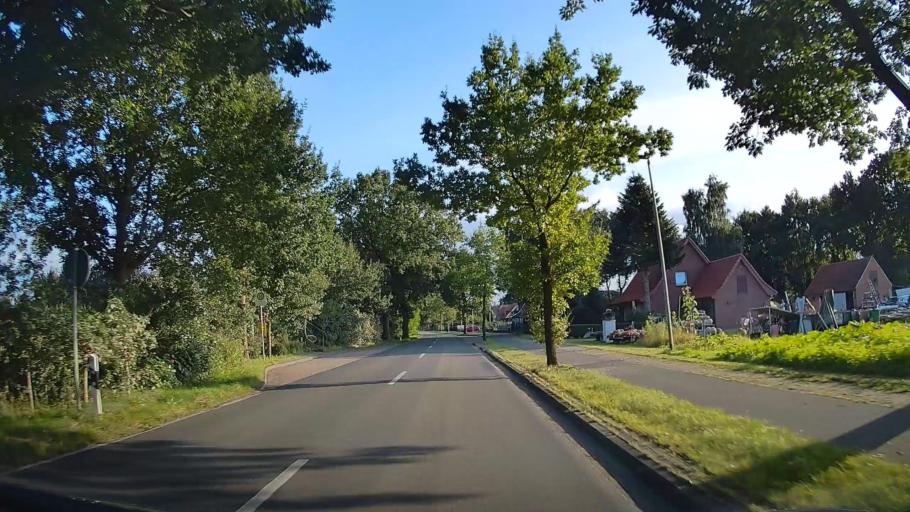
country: DE
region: Lower Saxony
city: Hilkenbrook
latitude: 53.0315
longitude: 7.7460
